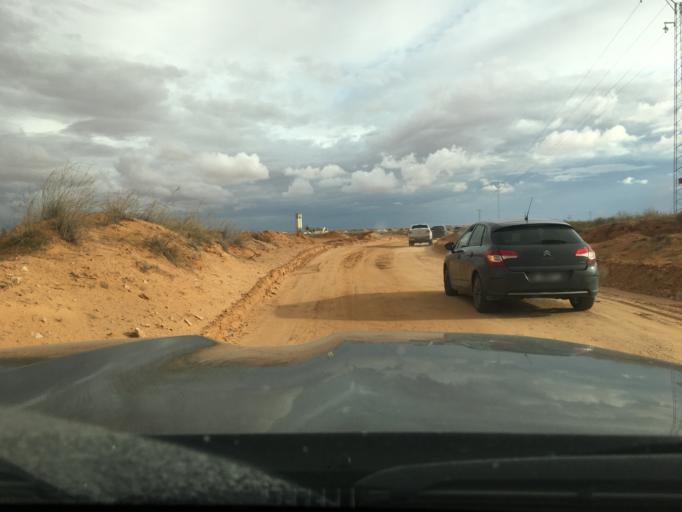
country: TN
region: Madanin
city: Medenine
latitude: 33.2708
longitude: 10.5675
